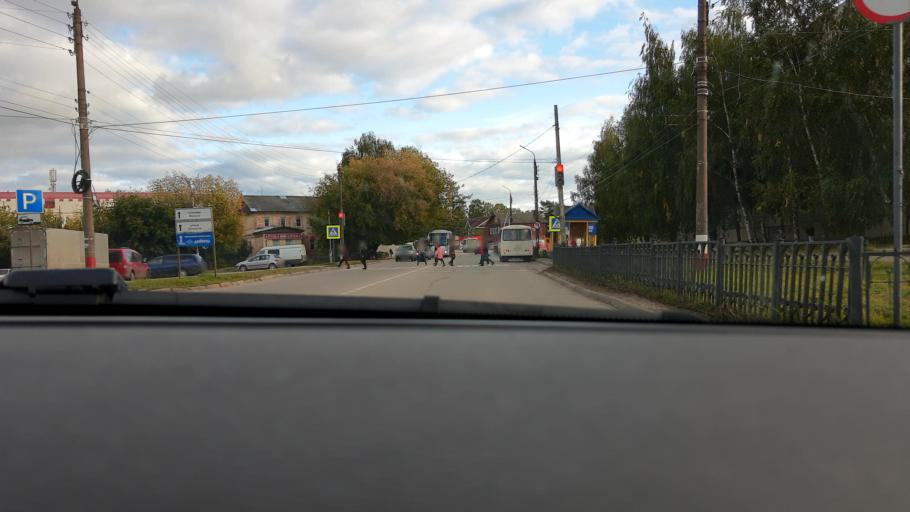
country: RU
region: Nizjnij Novgorod
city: Novaya Balakhna
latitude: 56.4951
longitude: 43.6086
